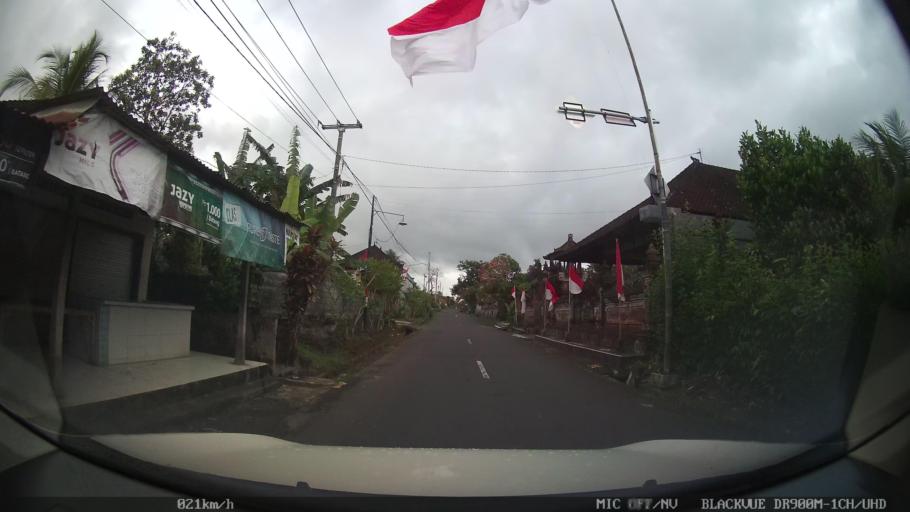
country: ID
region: Bali
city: Banjar Cemenggon
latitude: -8.5390
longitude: 115.1913
